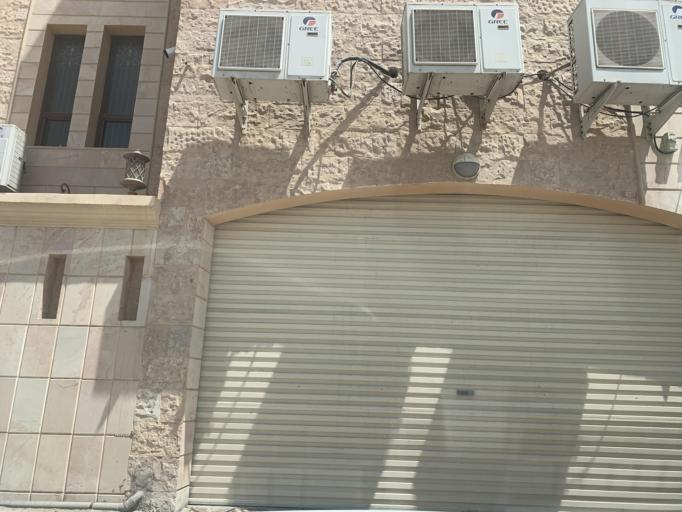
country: BH
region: Manama
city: Jidd Hafs
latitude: 26.2179
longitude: 50.5350
